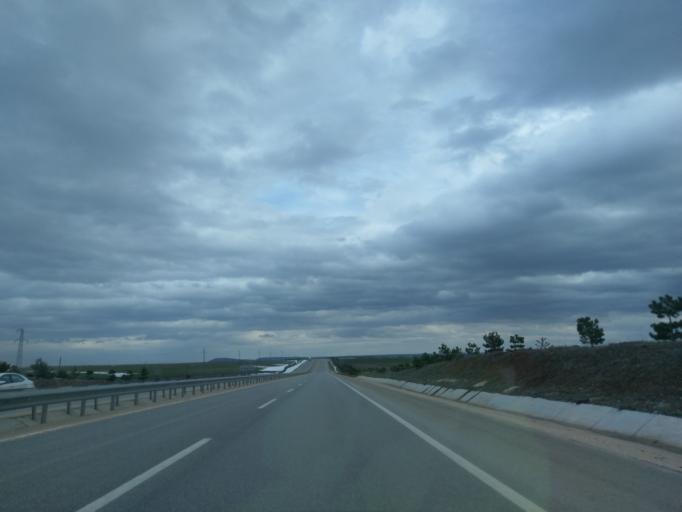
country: TR
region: Eskisehir
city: Inonu
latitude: 39.7259
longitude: 30.3044
